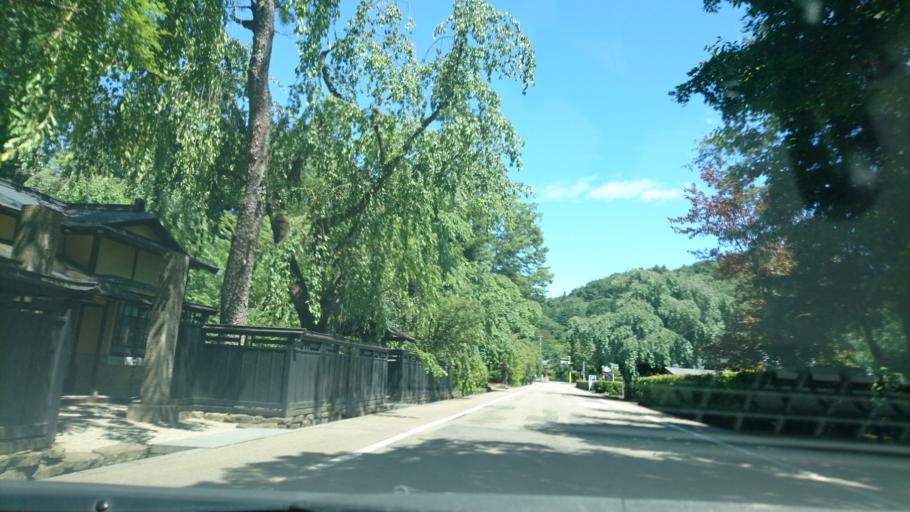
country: JP
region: Akita
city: Kakunodatemachi
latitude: 39.6012
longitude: 140.5613
